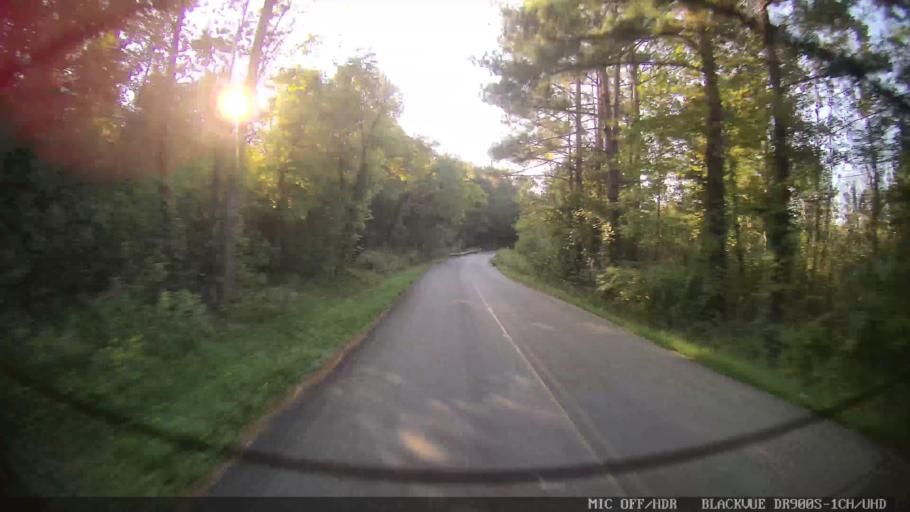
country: US
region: Tennessee
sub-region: Bradley County
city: Wildwood Lake
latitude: 35.0247
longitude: -84.7735
